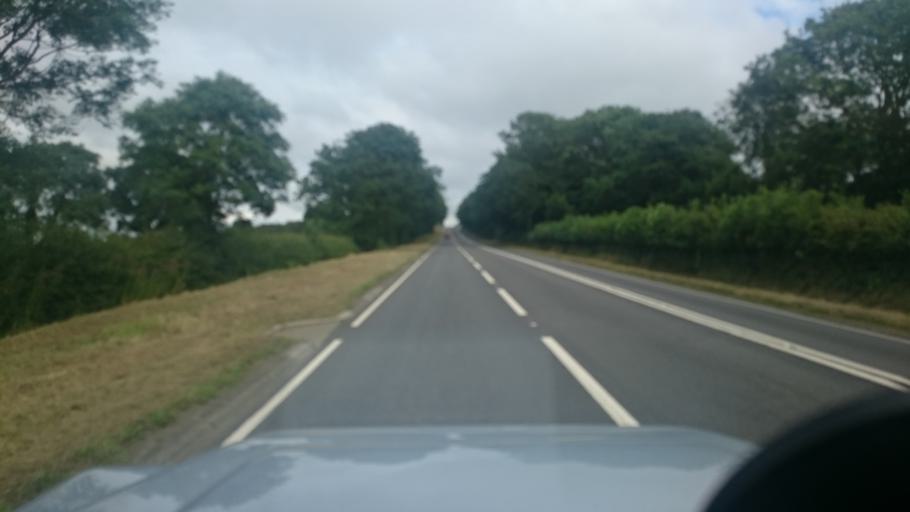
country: GB
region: Wales
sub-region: Pembrokeshire
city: Wiston
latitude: 51.8049
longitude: -4.8953
